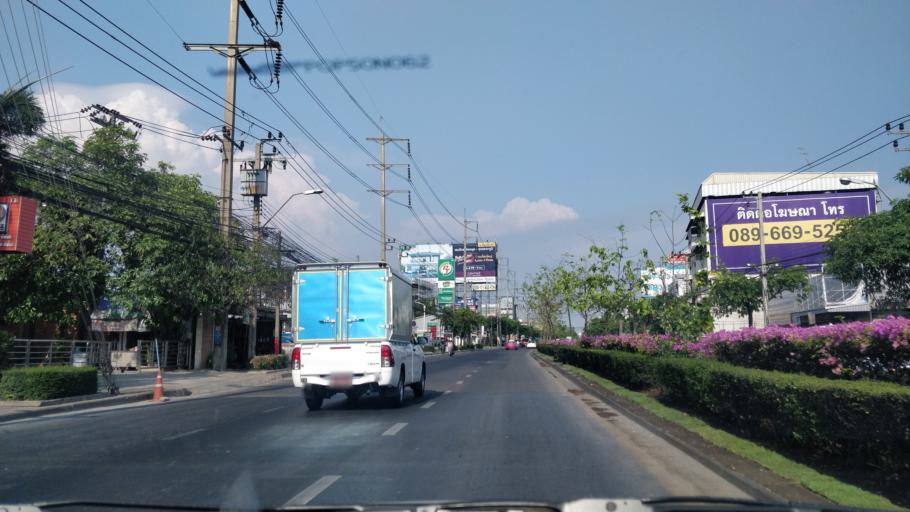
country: TH
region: Bangkok
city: Suan Luang
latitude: 13.7202
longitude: 100.6789
